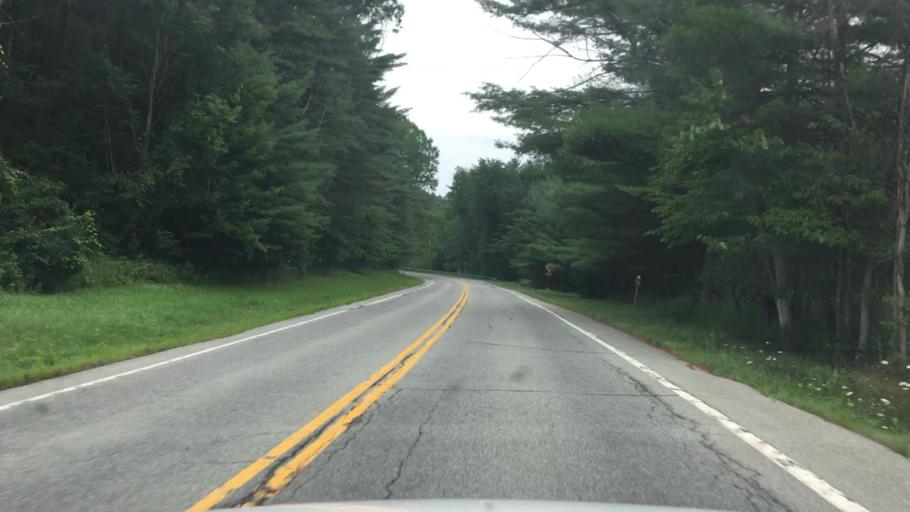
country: US
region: New York
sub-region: Essex County
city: Keeseville
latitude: 44.4176
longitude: -73.6799
